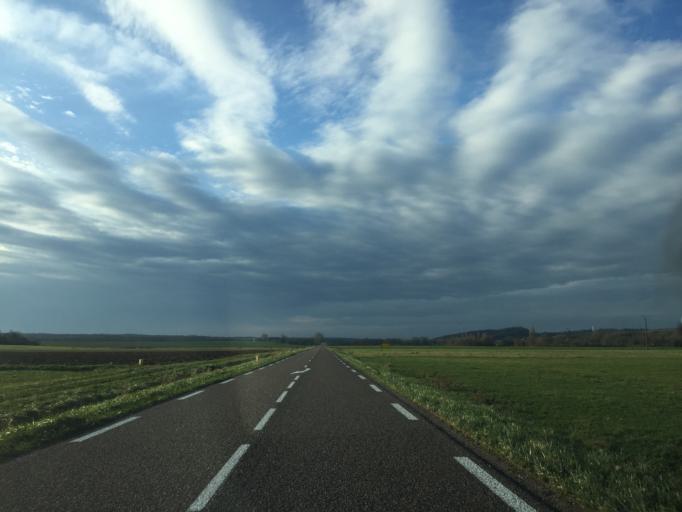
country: FR
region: Franche-Comte
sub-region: Departement du Jura
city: Arbois
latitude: 46.9175
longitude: 5.7378
